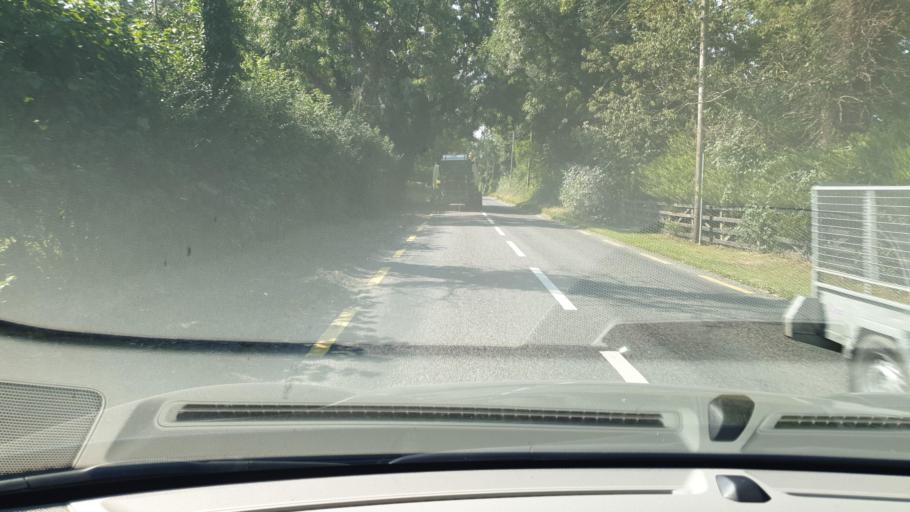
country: IE
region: Leinster
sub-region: An Mhi
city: Trim
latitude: 53.5811
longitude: -6.8451
